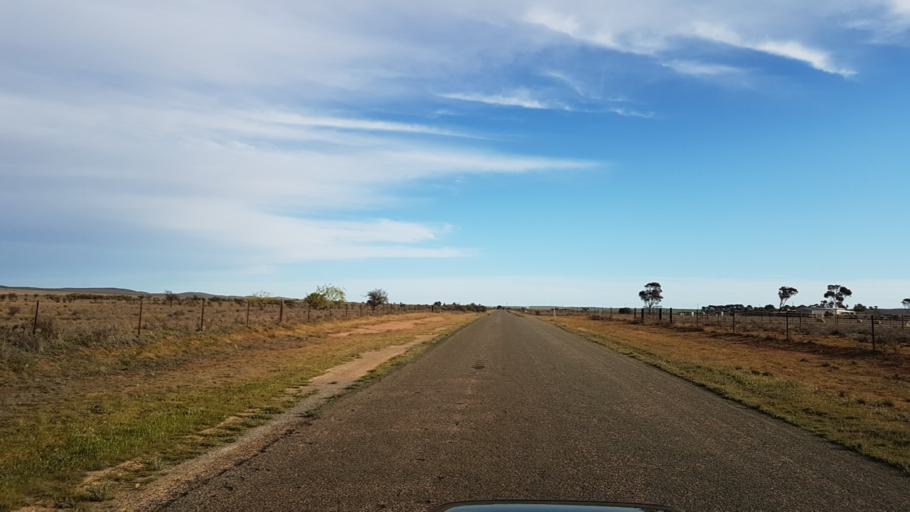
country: AU
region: South Australia
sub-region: Peterborough
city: Peterborough
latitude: -32.9849
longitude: 138.8507
